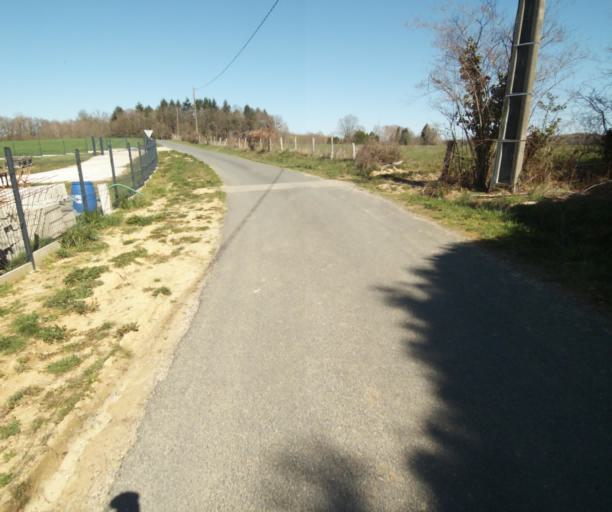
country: FR
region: Limousin
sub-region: Departement de la Correze
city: Saint-Mexant
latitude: 45.3074
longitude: 1.6537
